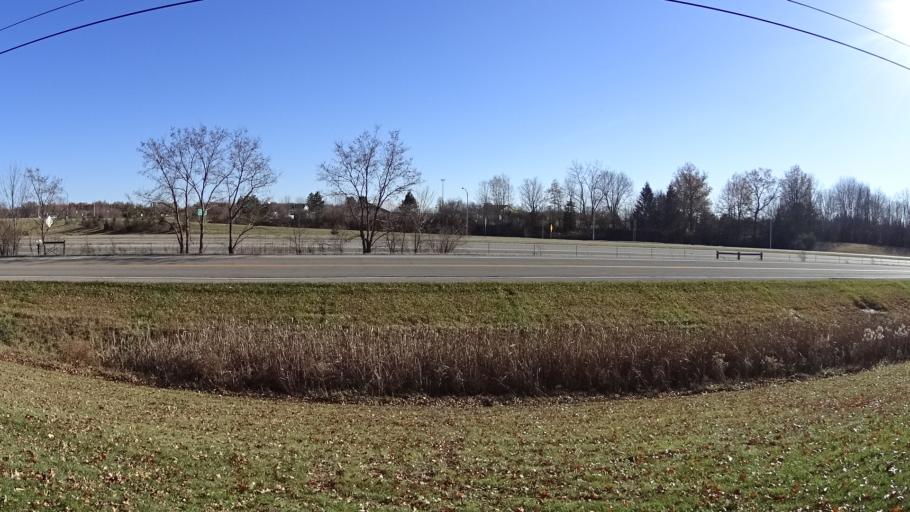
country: US
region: Ohio
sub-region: Lorain County
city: Elyria
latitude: 41.3178
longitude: -82.1206
